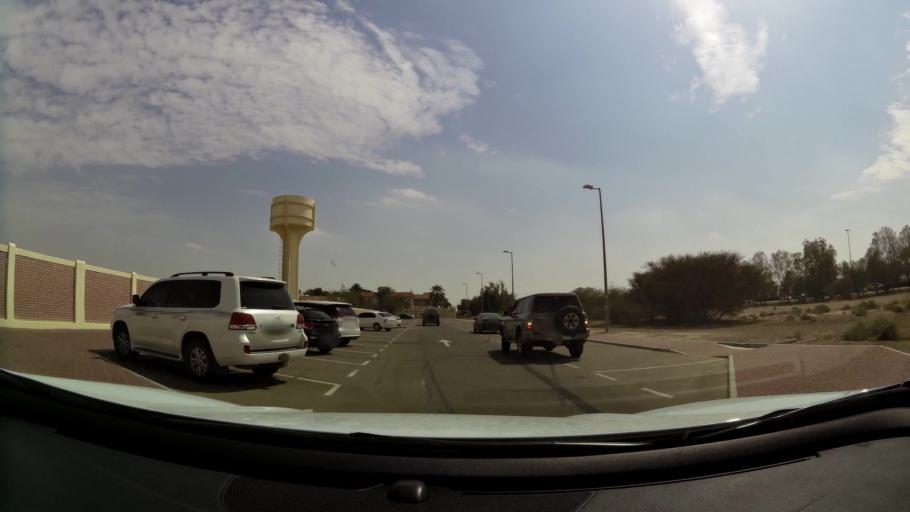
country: AE
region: Abu Dhabi
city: Al Ain
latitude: 24.1917
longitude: 55.7905
